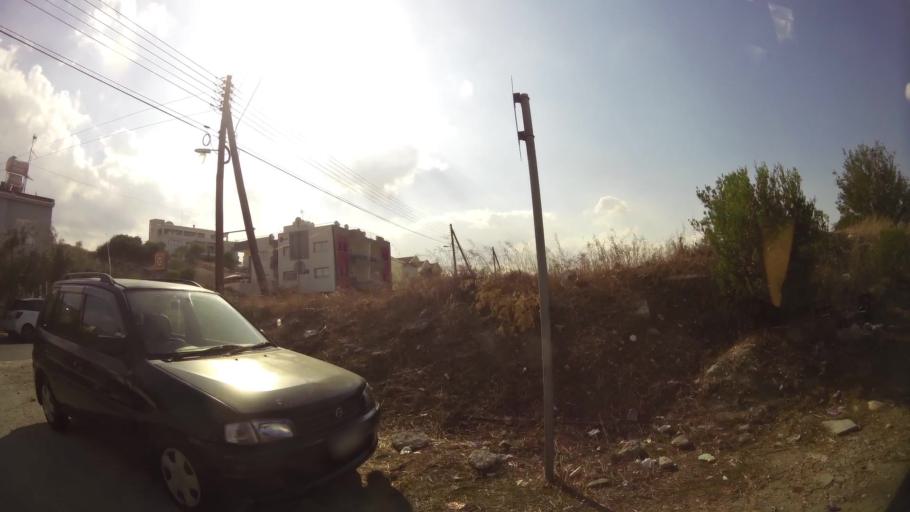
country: CY
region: Lefkosia
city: Nicosia
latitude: 35.1513
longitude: 33.3036
